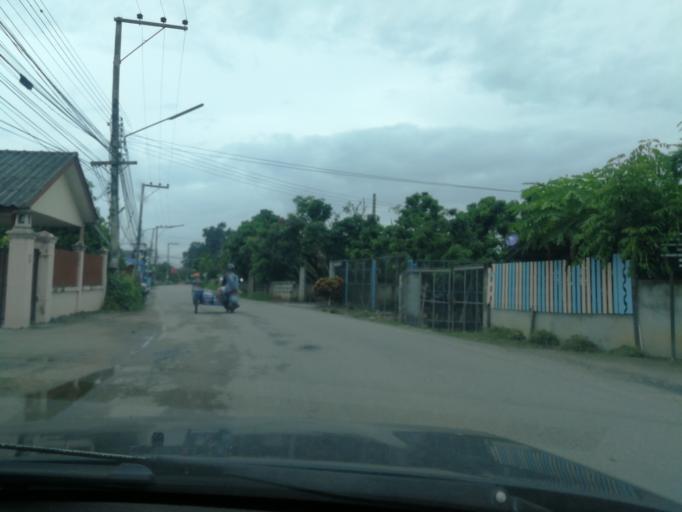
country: TH
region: Chiang Mai
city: San Pa Tong
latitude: 18.6115
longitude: 98.9049
